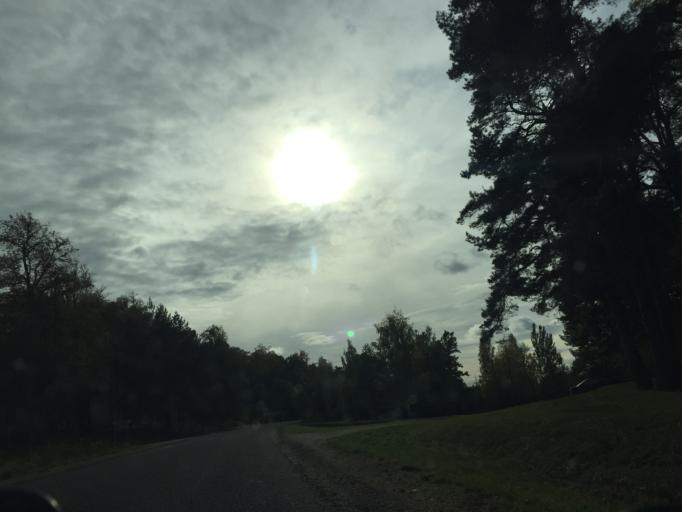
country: LV
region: Auces Novads
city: Auce
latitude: 56.5536
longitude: 23.0174
